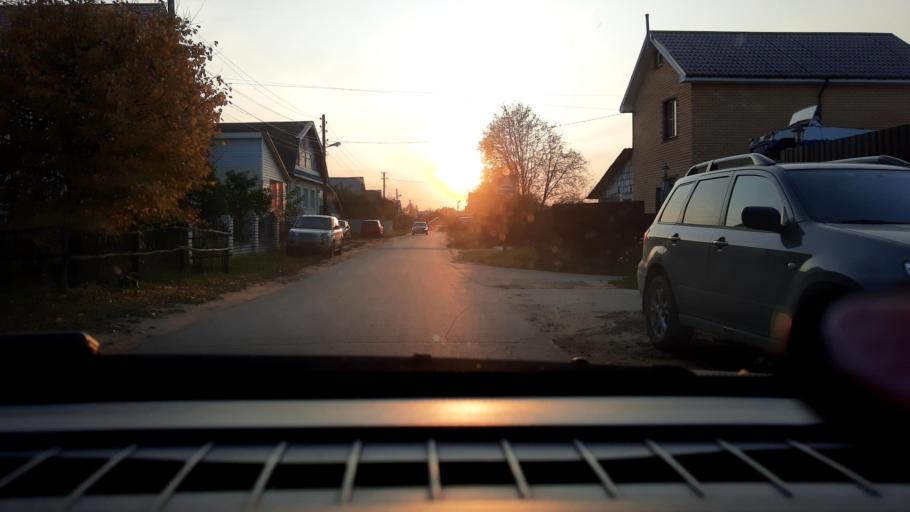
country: RU
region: Nizjnij Novgorod
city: Neklyudovo
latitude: 56.4000
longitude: 44.0272
